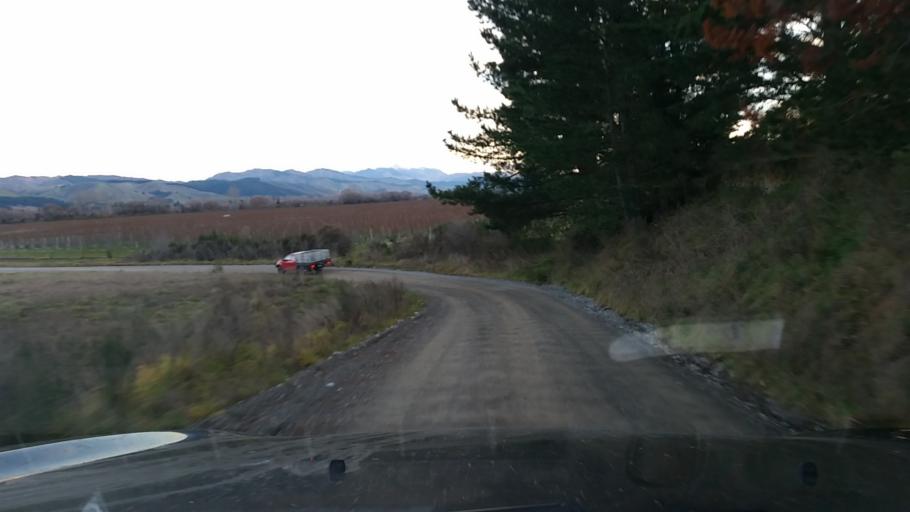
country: NZ
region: Marlborough
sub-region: Marlborough District
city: Blenheim
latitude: -41.5195
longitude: 173.5820
